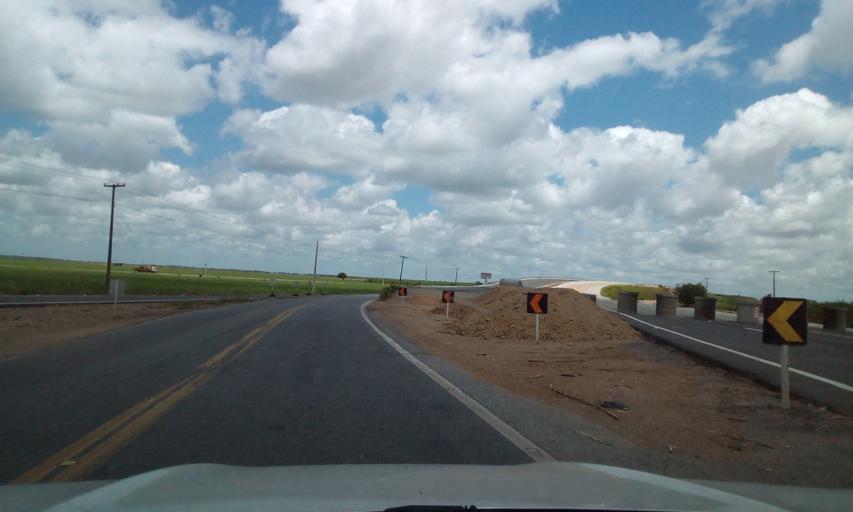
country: BR
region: Alagoas
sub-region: Campo Alegre
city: Campo Alegre
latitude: -9.9002
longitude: -36.3004
